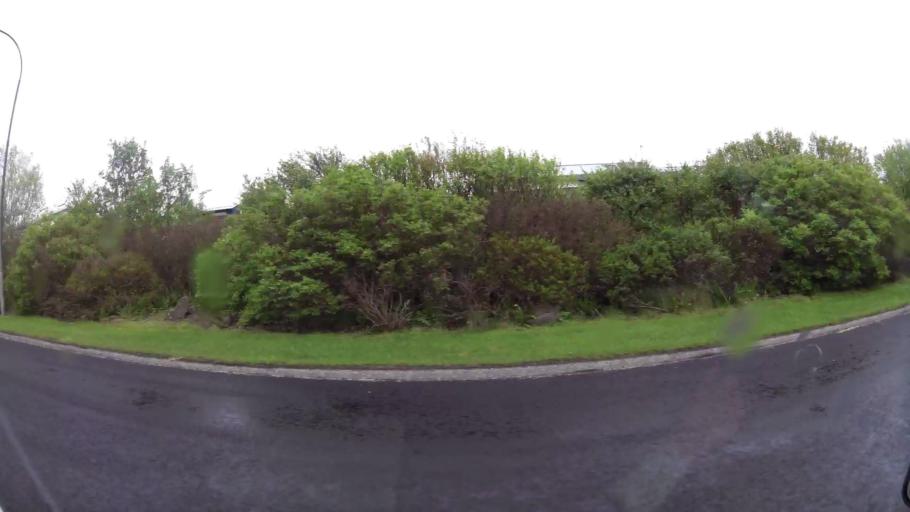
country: IS
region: Capital Region
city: Kopavogur
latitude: 64.0947
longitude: -21.9005
